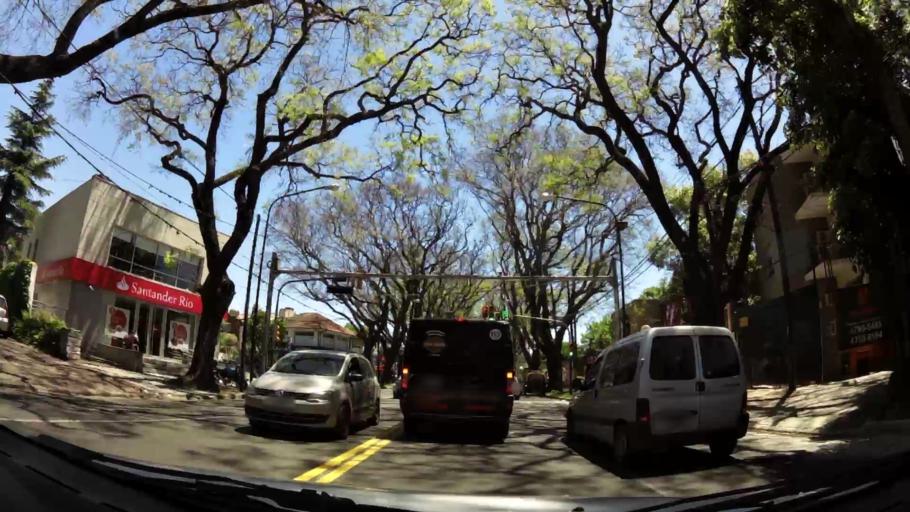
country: AR
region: Buenos Aires
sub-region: Partido de San Isidro
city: San Isidro
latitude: -34.4763
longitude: -58.4990
